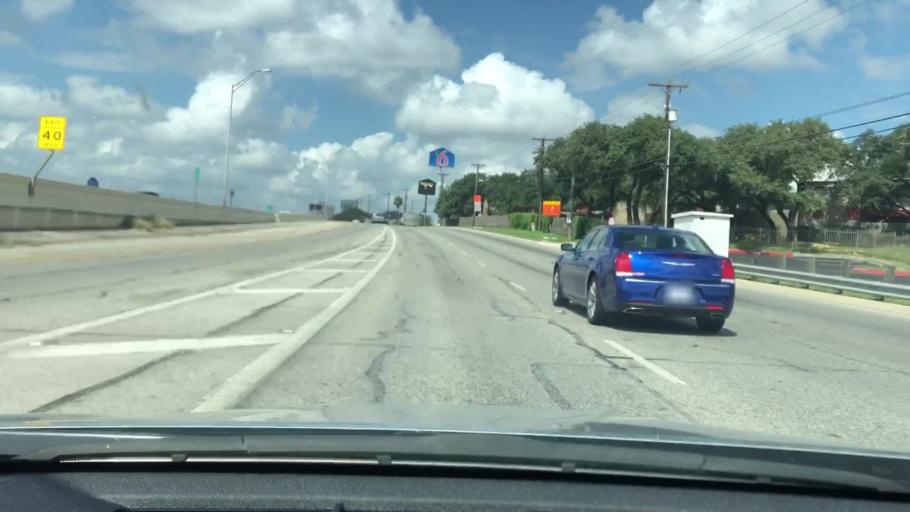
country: US
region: Texas
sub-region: Bexar County
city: Balcones Heights
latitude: 29.5257
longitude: -98.5564
